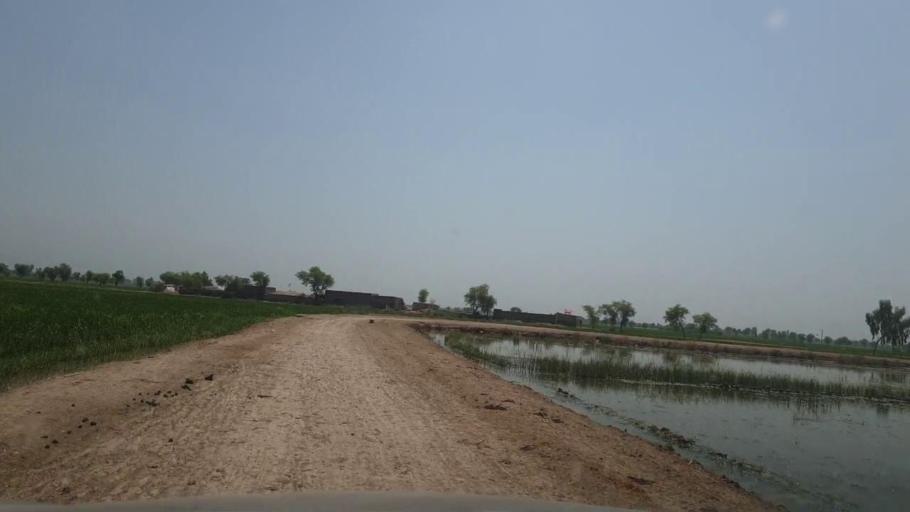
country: PK
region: Sindh
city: Warah
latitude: 27.5166
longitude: 67.7774
